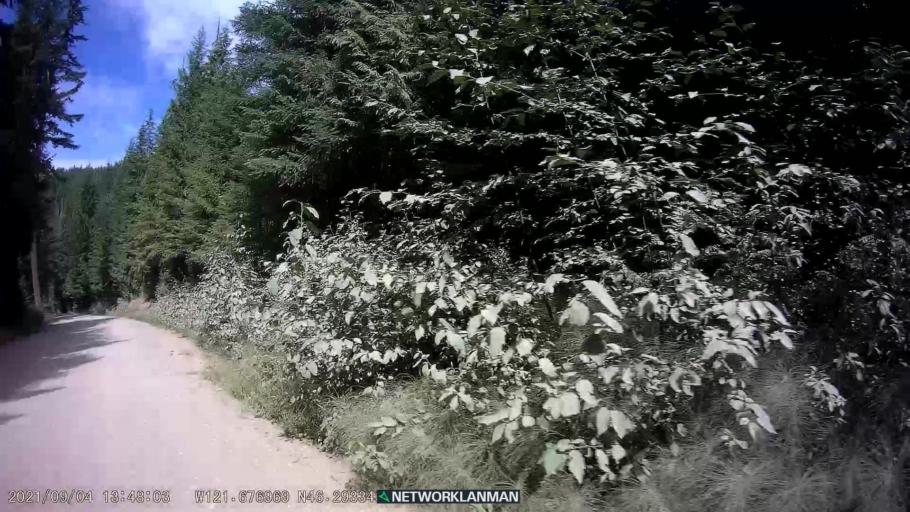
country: US
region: Washington
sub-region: Skamania County
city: Carson
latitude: 46.2936
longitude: -121.6768
